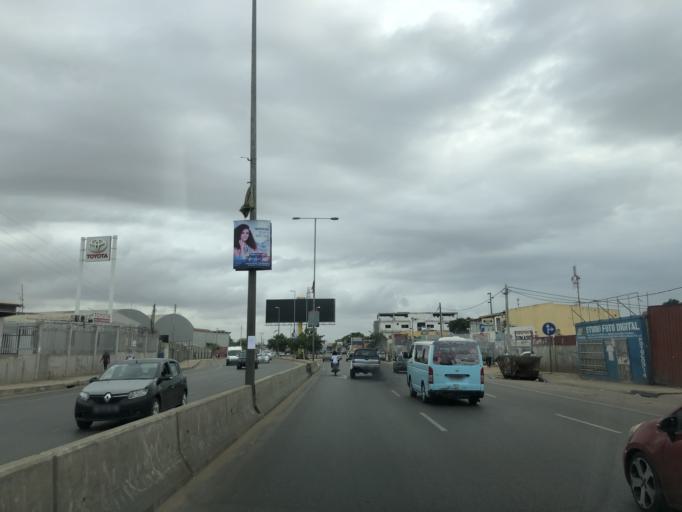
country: AO
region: Luanda
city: Luanda
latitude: -8.8720
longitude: 13.2115
